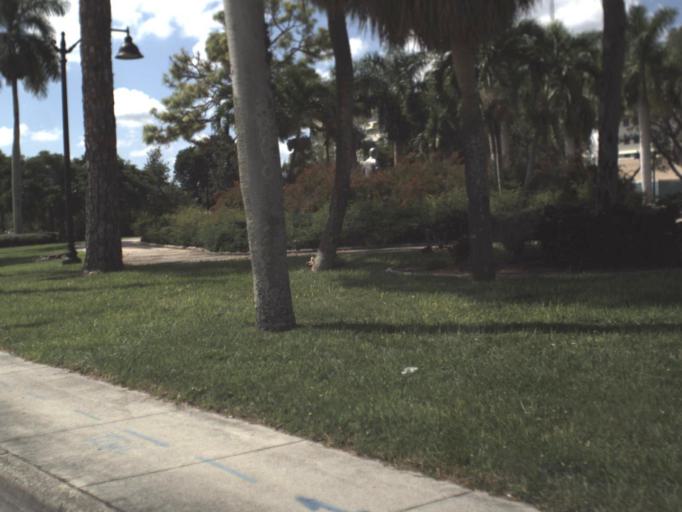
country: US
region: Florida
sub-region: Lee County
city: Fort Myers
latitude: 26.6296
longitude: -81.8725
